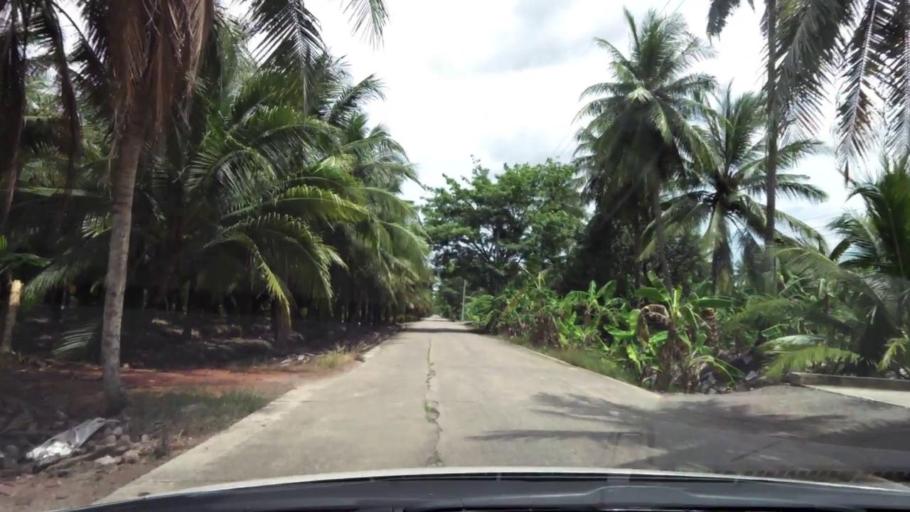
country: TH
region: Ratchaburi
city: Damnoen Saduak
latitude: 13.5254
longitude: 100.0041
